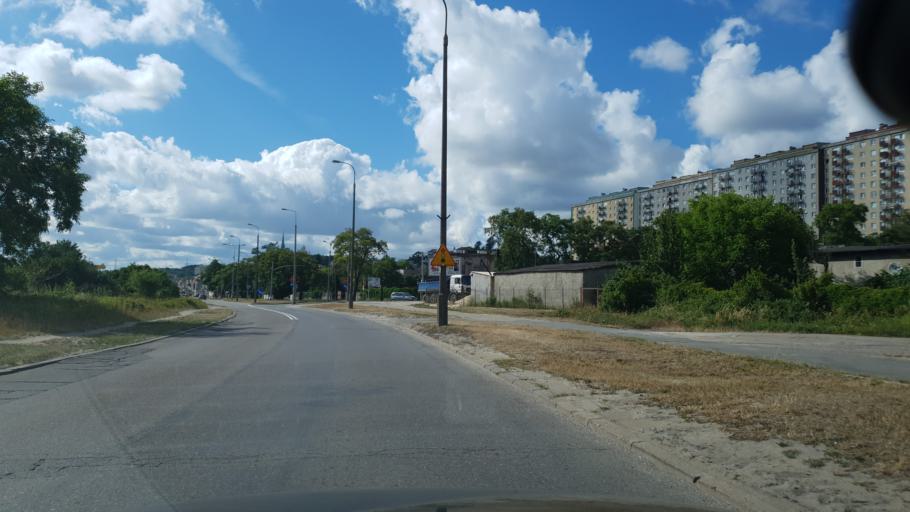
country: PL
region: Pomeranian Voivodeship
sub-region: Gdynia
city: Gdynia
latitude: 54.5478
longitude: 18.5182
